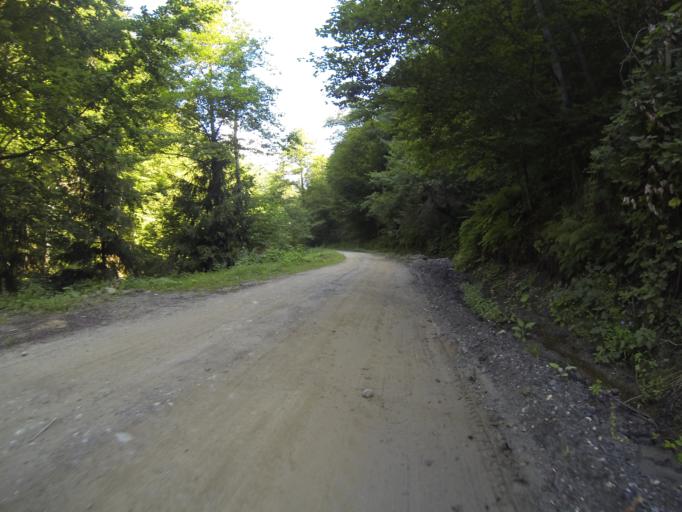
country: RO
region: Valcea
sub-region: Comuna Costesti
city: Bistrita
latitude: 45.2221
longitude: 24.0035
